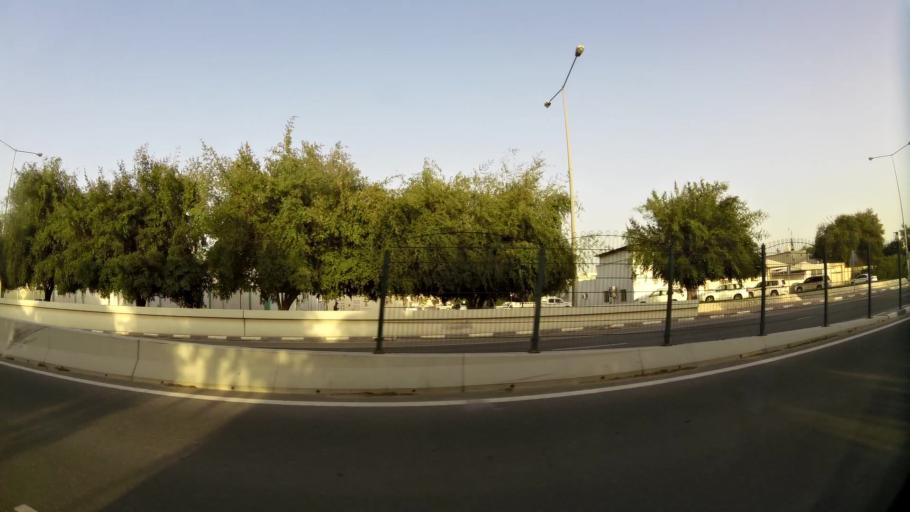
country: QA
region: Baladiyat ar Rayyan
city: Ar Rayyan
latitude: 25.3170
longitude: 51.4602
